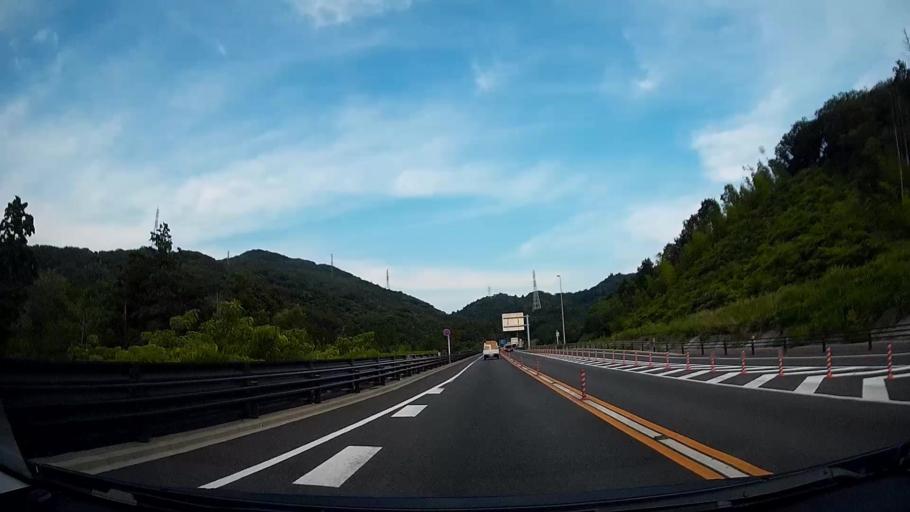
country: JP
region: Aichi
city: Gamagori
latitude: 34.8538
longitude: 137.1865
